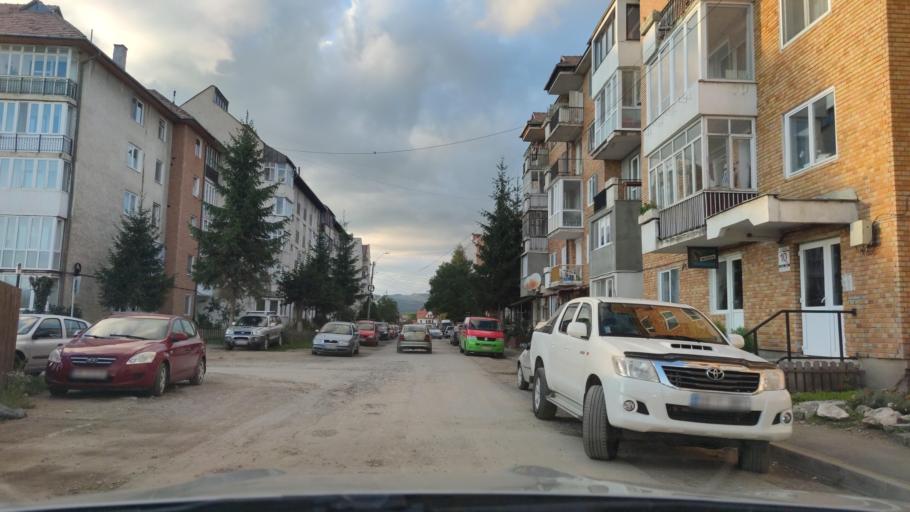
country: RO
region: Harghita
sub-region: Municipiul Gheorgheni
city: Gheorgheni
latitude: 46.7199
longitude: 25.5871
